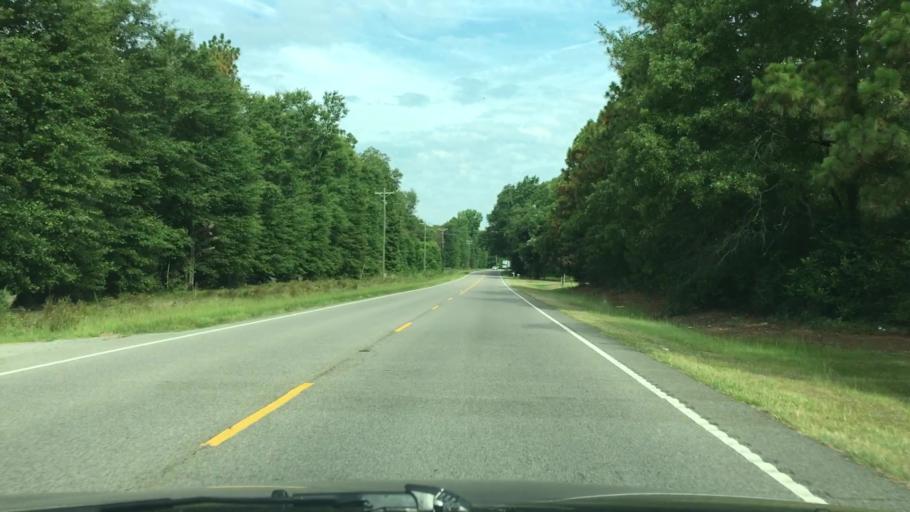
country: US
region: South Carolina
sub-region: Barnwell County
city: Williston
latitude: 33.6605
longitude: -81.3866
